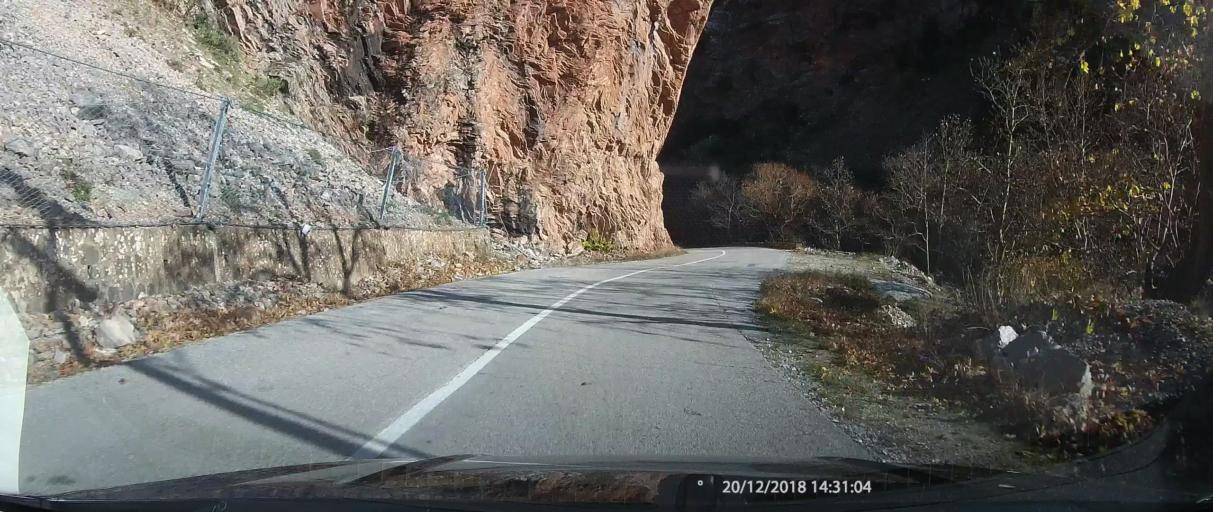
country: GR
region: Central Greece
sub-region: Nomos Evrytanias
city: Karpenisi
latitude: 38.7932
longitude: 21.7023
